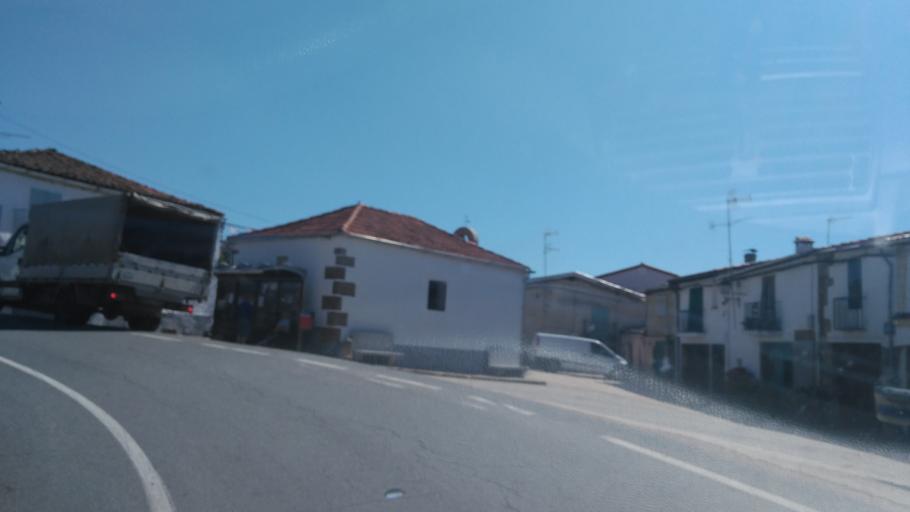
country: ES
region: Castille and Leon
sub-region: Provincia de Salamanca
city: San Martin del Castanar
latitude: 40.5373
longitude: -6.0458
